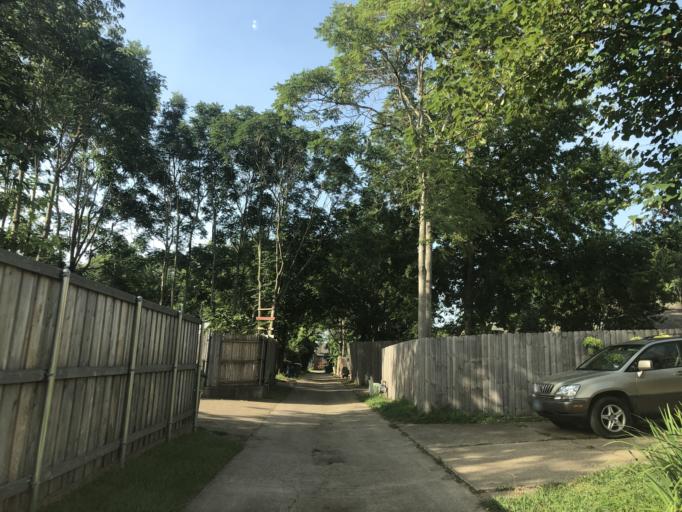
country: US
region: Texas
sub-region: Dallas County
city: Sunnyvale
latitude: 32.8369
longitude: -96.5862
